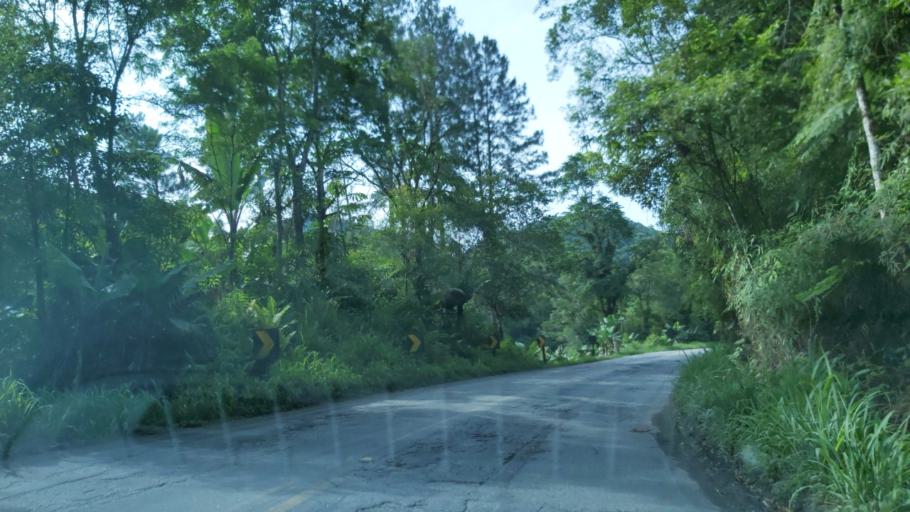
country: BR
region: Sao Paulo
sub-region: Miracatu
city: Miracatu
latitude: -24.0545
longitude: -47.5768
